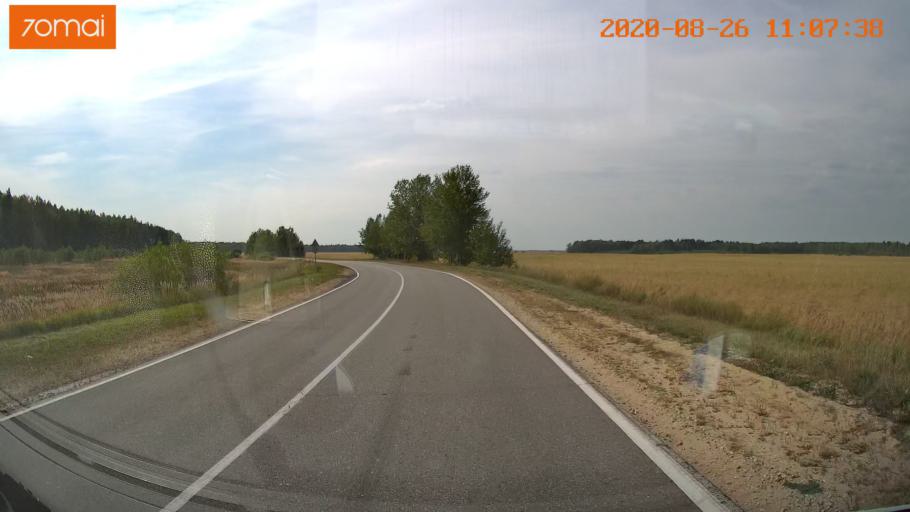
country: RU
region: Rjazan
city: Izhevskoye
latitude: 54.5165
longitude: 41.1212
